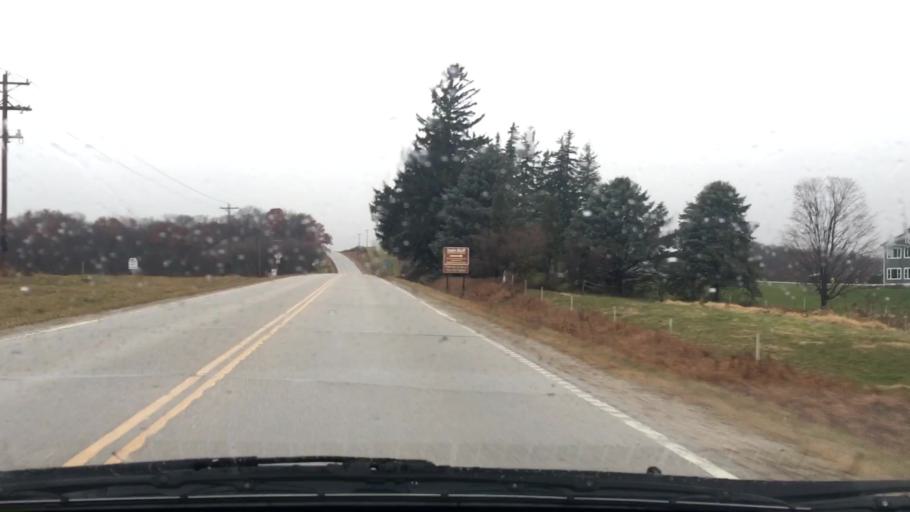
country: US
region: Minnesota
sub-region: Fillmore County
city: Preston
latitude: 43.7333
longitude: -92.0027
